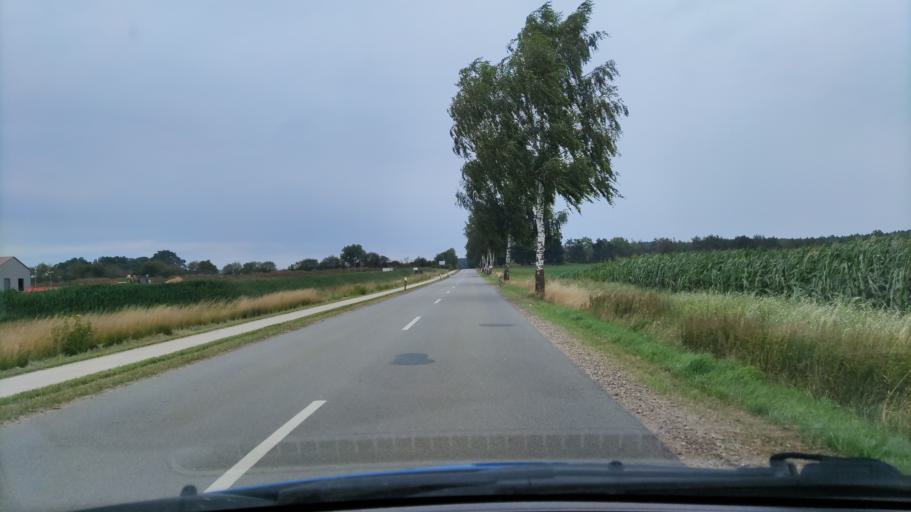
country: DE
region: Lower Saxony
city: Rosche
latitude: 52.9904
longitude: 10.7645
